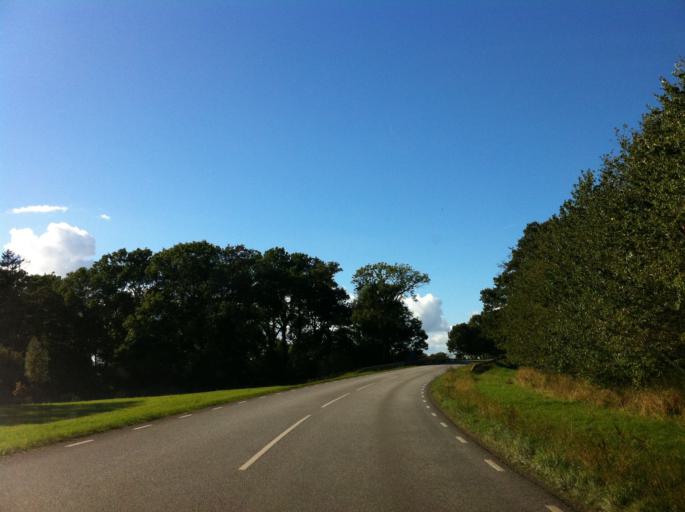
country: SE
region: Skane
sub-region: Sjobo Kommun
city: Blentarp
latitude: 55.6999
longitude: 13.5879
